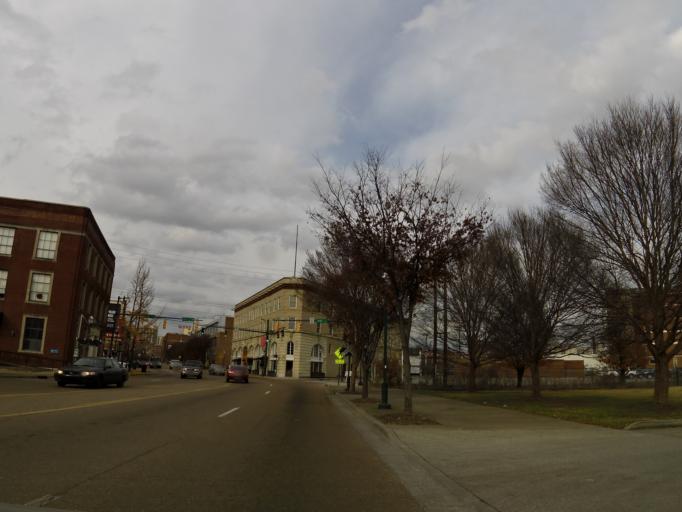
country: US
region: Tennessee
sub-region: Hamilton County
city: Chattanooga
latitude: 35.0390
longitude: -85.3074
